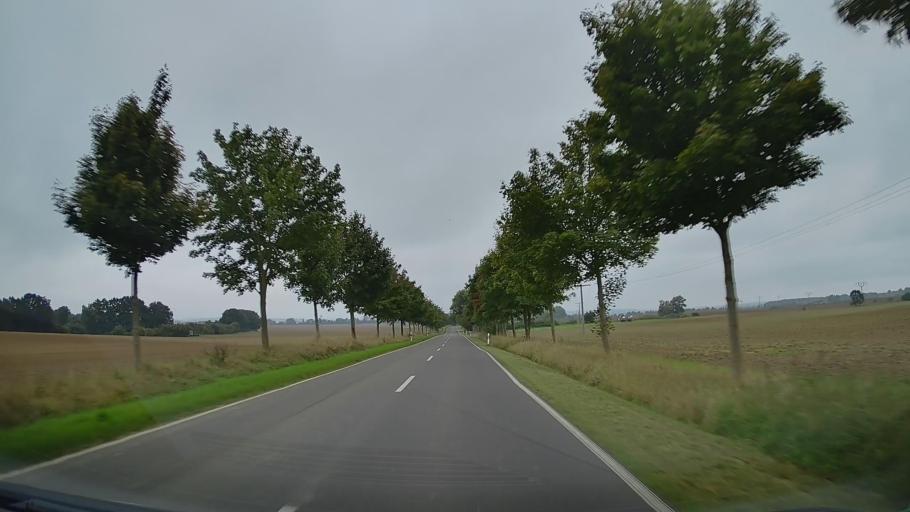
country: DE
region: Mecklenburg-Vorpommern
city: Guestrow
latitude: 53.7991
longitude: 12.1008
